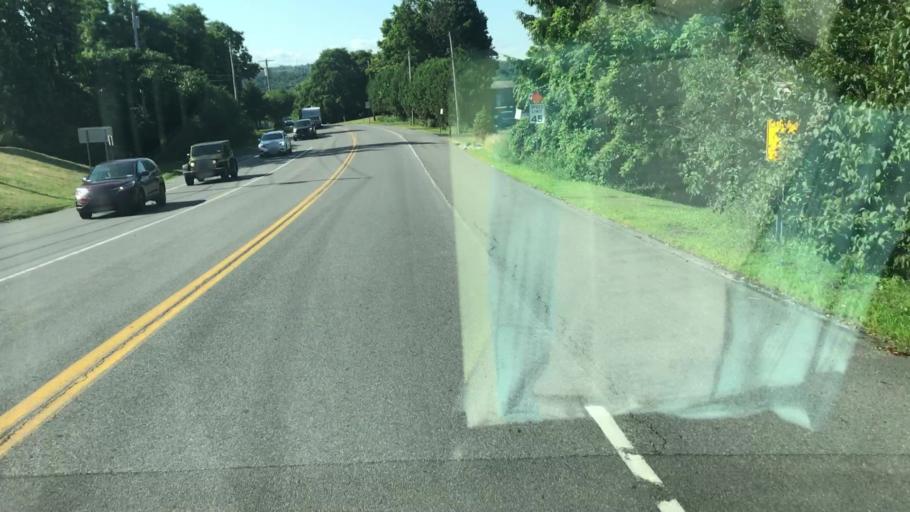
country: US
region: New York
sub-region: Onondaga County
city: Marcellus
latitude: 43.0344
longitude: -76.3653
